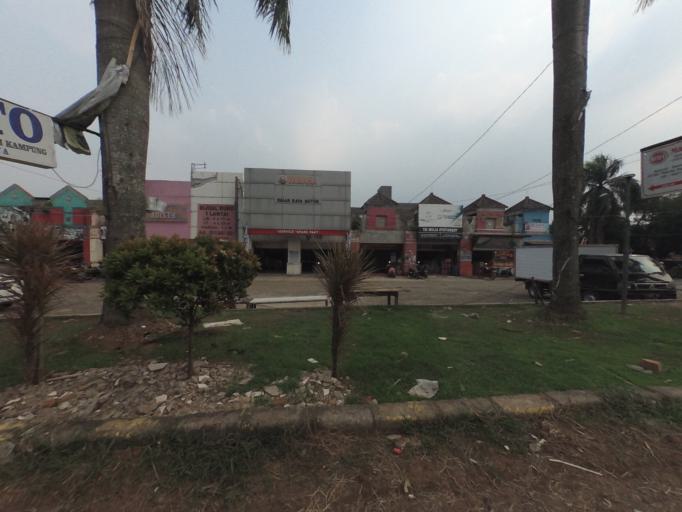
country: ID
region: West Java
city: Ciampea
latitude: -6.5592
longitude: 106.6914
